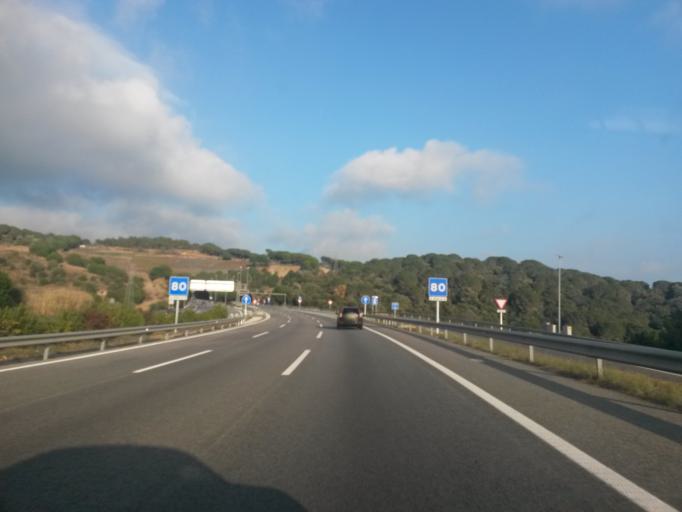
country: ES
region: Catalonia
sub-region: Provincia de Barcelona
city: Canet de Mar
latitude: 41.5956
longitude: 2.5709
